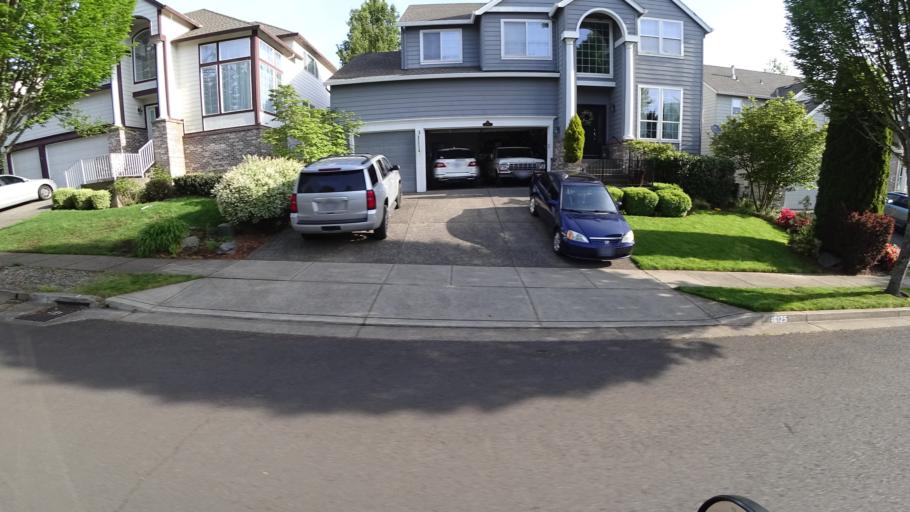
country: US
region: Oregon
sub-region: Washington County
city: King City
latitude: 45.4314
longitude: -122.8426
